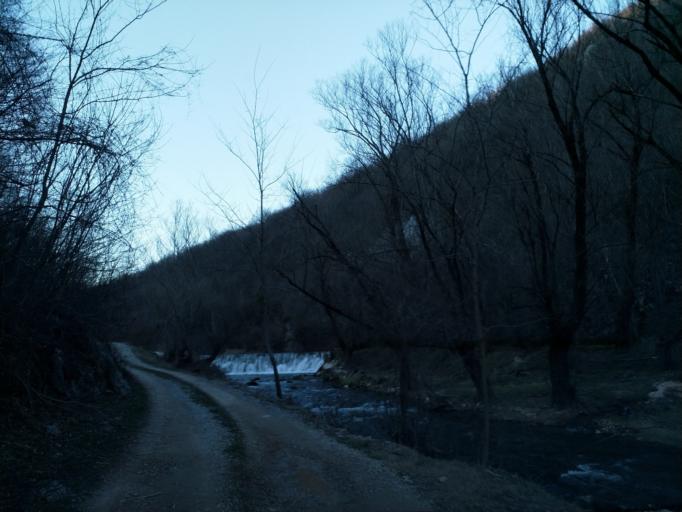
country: RS
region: Central Serbia
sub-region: Pomoravski Okrug
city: Paracin
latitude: 43.9251
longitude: 21.5256
